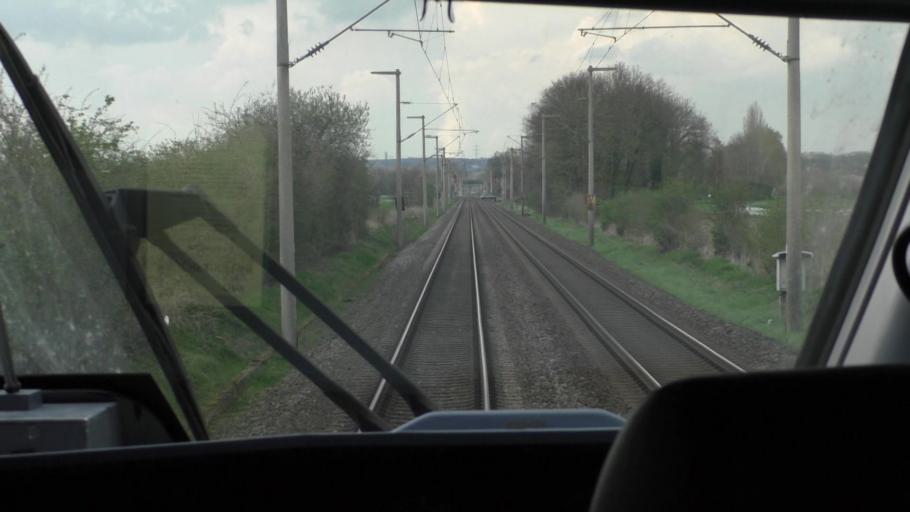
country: DE
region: North Rhine-Westphalia
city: Wesseling
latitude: 50.8060
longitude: 6.9427
